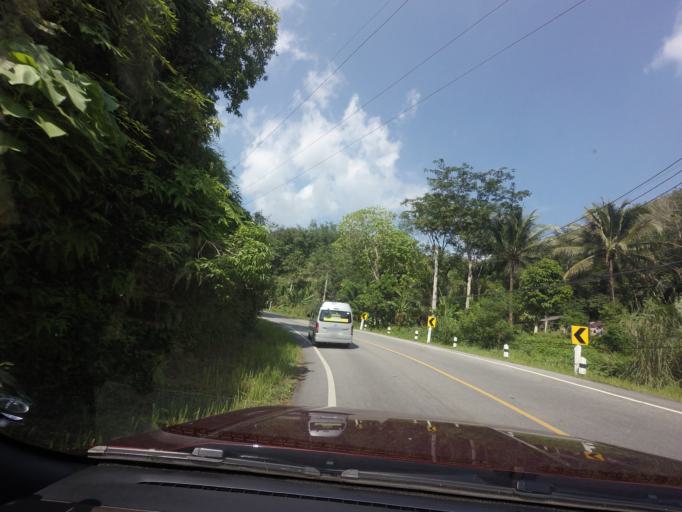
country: TH
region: Yala
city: Betong
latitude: 5.9358
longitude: 101.1857
